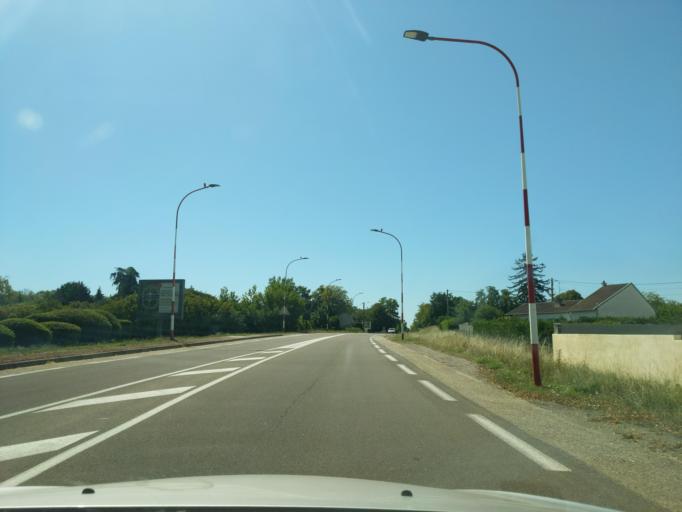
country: FR
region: Bourgogne
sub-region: Departement de la Cote-d'Or
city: Sennecey-les-Dijon
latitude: 47.2881
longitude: 5.0981
